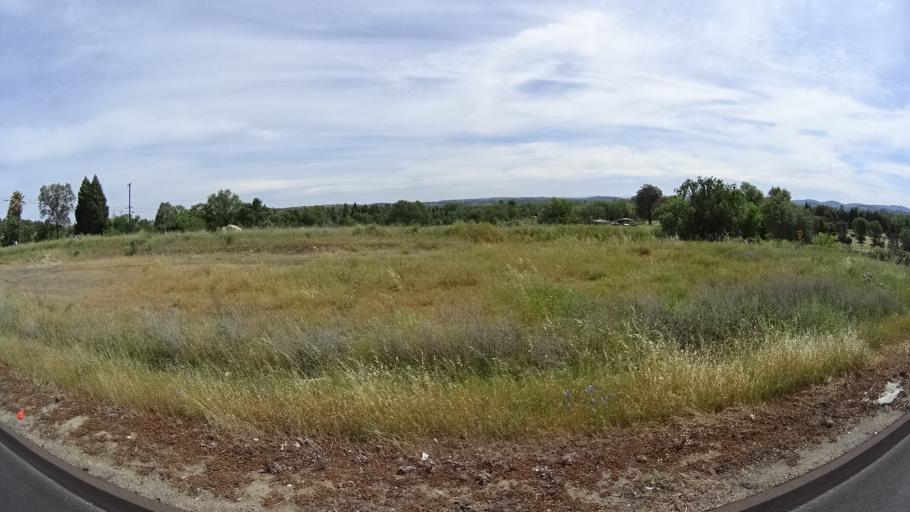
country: US
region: California
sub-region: Placer County
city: Loomis
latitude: 38.8350
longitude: -121.2195
